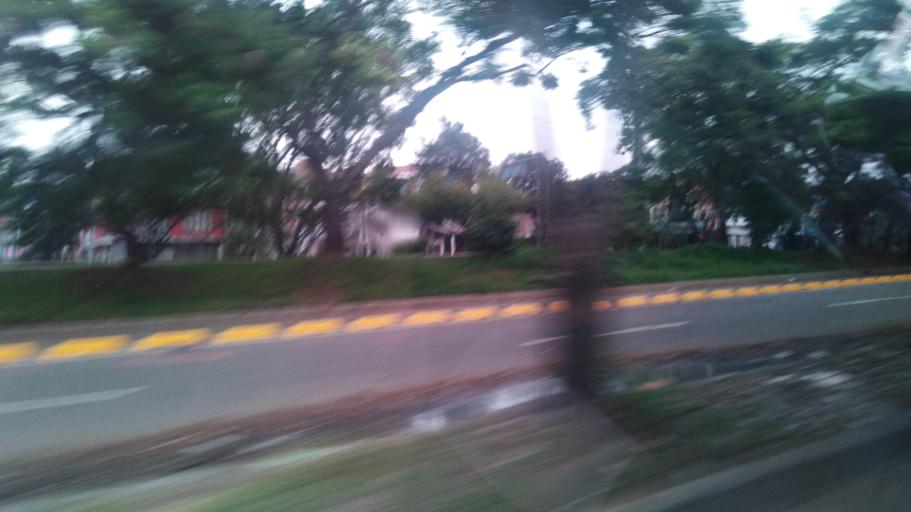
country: CO
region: Valle del Cauca
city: Cali
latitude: 3.4208
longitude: -76.5064
